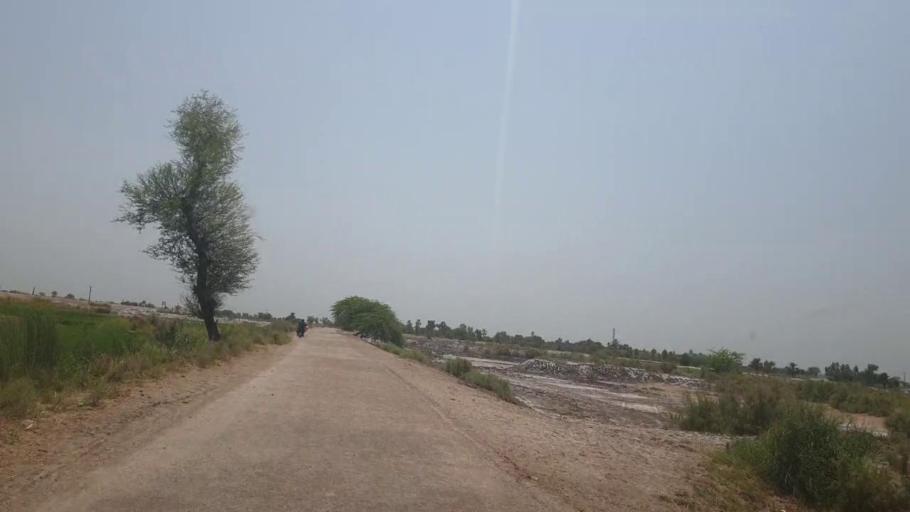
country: PK
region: Sindh
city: Lakhi
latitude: 27.8654
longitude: 68.6625
